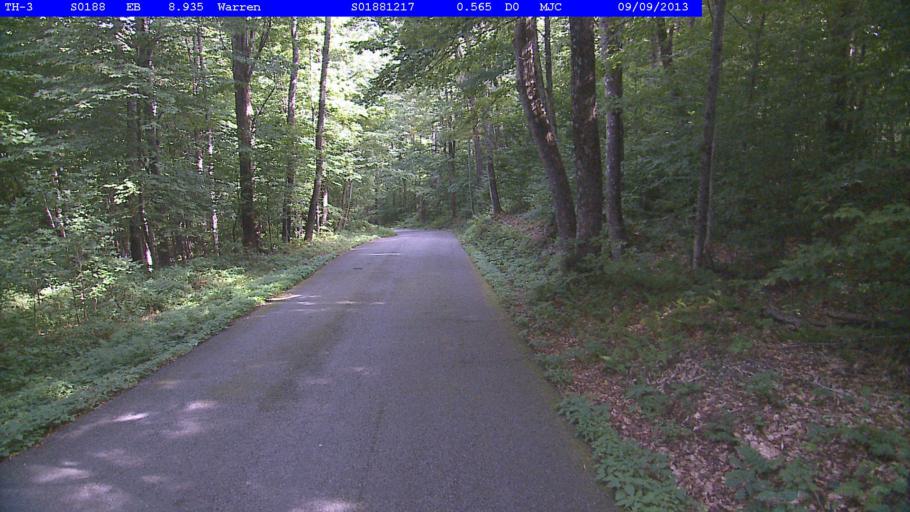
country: US
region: Vermont
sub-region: Addison County
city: Bristol
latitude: 44.0919
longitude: -72.9137
